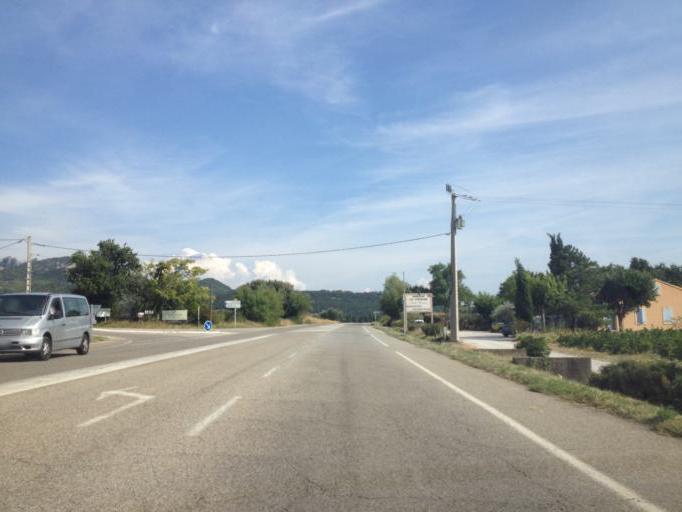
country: FR
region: Provence-Alpes-Cote d'Azur
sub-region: Departement du Vaucluse
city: Violes
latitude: 44.1641
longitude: 4.9738
